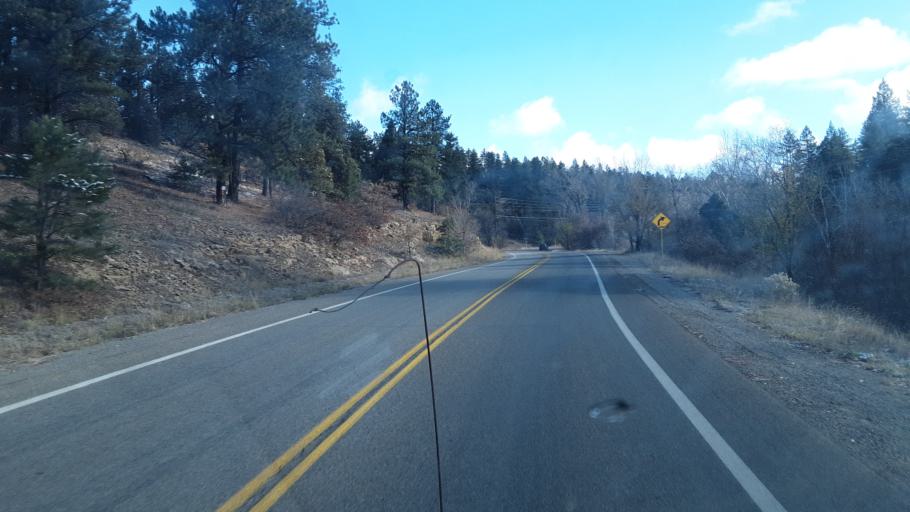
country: US
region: Colorado
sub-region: La Plata County
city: Durango
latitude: 37.3045
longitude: -107.8322
